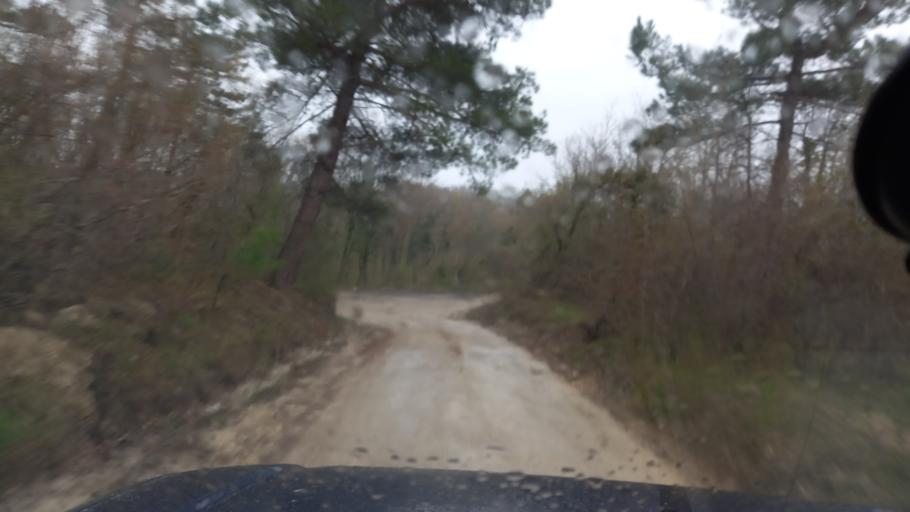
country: RU
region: Krasnodarskiy
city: Dzhubga
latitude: 44.3164
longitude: 38.6876
